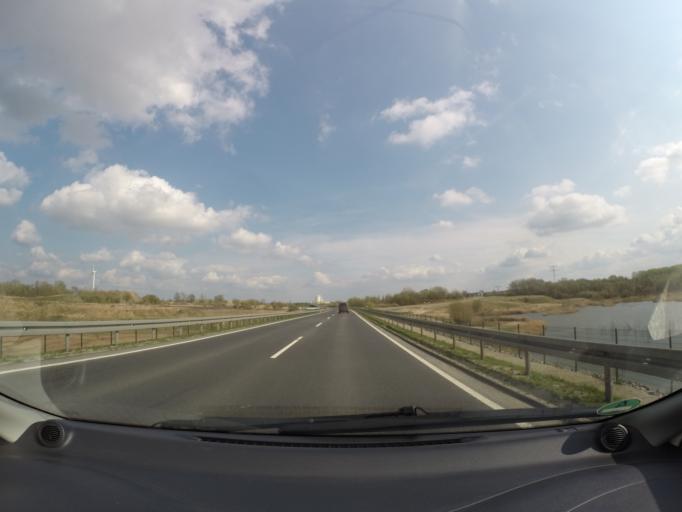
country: DE
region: Brandenburg
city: Rehfelde
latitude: 52.4887
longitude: 13.8519
